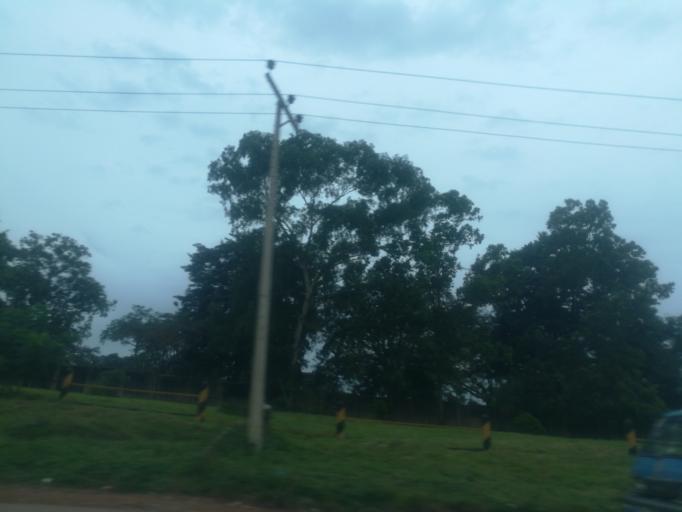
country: NG
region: Oyo
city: Ibadan
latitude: 7.3932
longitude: 3.9703
